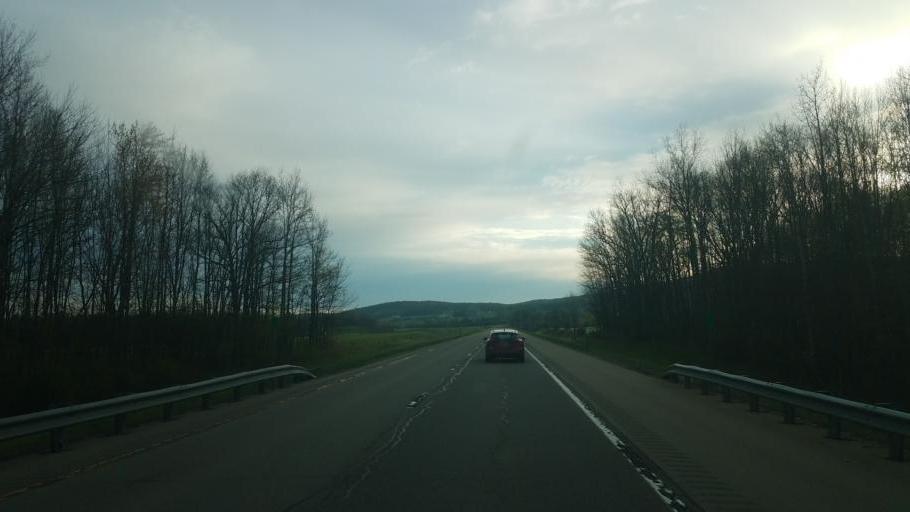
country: US
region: New York
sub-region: Allegany County
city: Belmont
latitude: 42.2766
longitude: -78.0422
